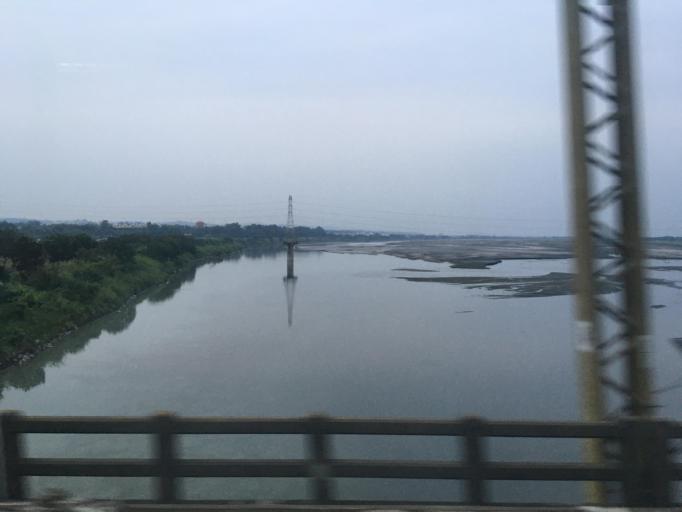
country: TW
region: Taiwan
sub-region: Pingtung
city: Pingtung
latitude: 22.6624
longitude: 120.4310
